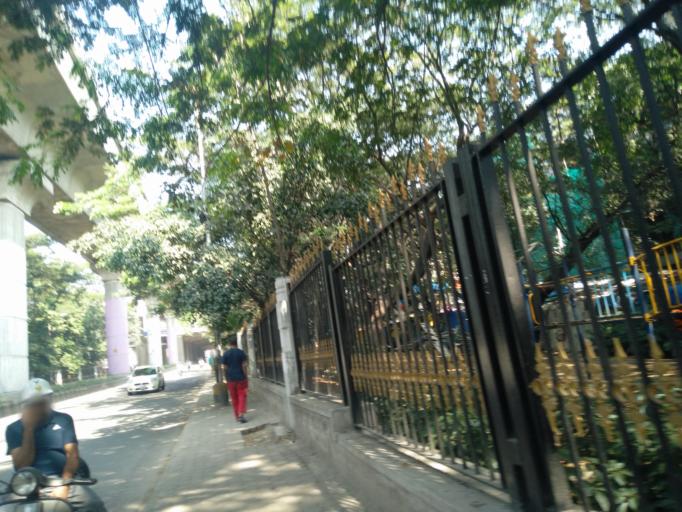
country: IN
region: Karnataka
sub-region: Bangalore Urban
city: Bangalore
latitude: 12.9691
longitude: 77.5369
